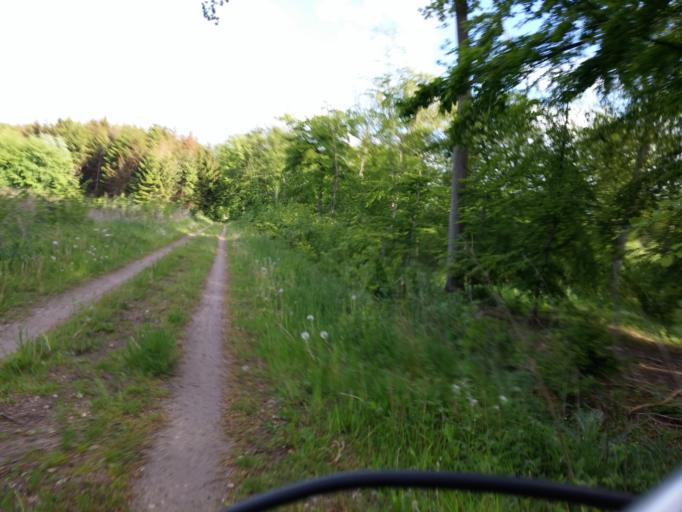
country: DK
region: South Denmark
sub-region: Kerteminde Kommune
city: Munkebo
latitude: 55.4283
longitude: 10.5481
